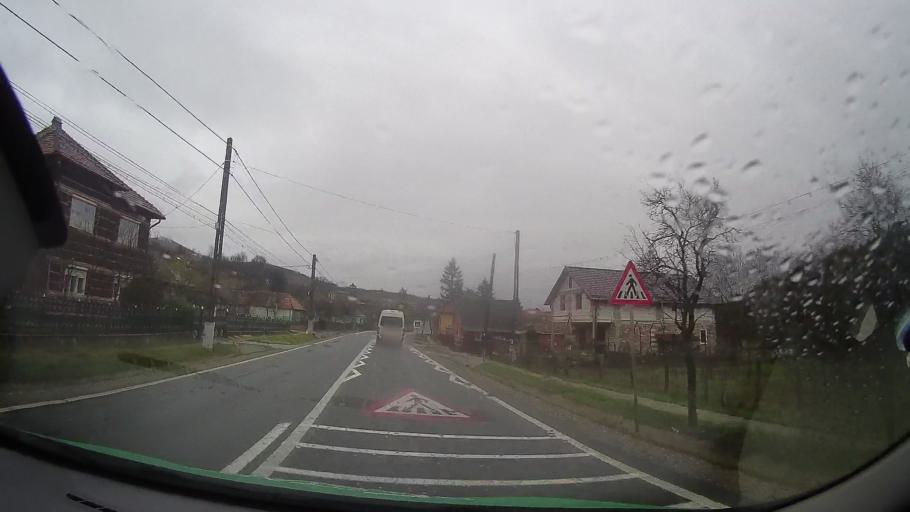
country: RO
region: Bistrita-Nasaud
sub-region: Comuna Galatii Bistritei
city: Galatii Bistritei
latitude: 47.0231
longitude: 24.4154
